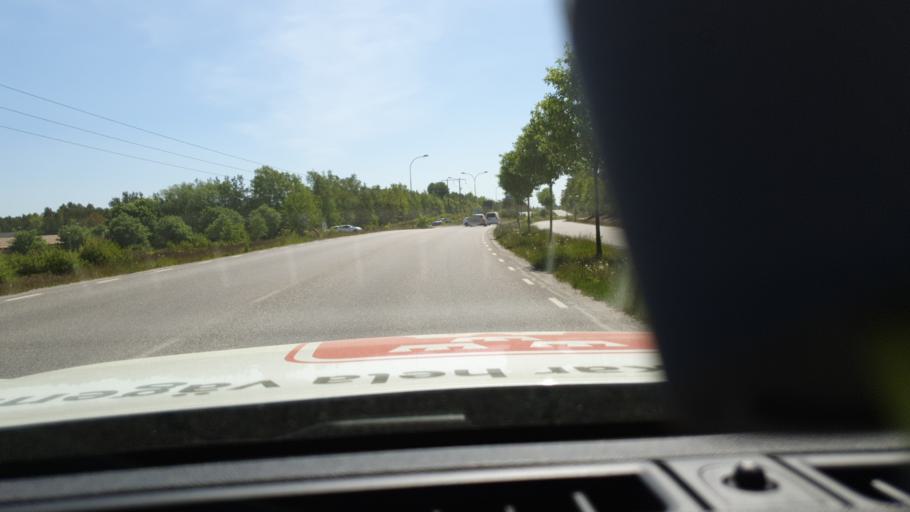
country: SE
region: Stockholm
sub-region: Nacka Kommun
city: Alta
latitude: 59.2438
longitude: 18.1955
